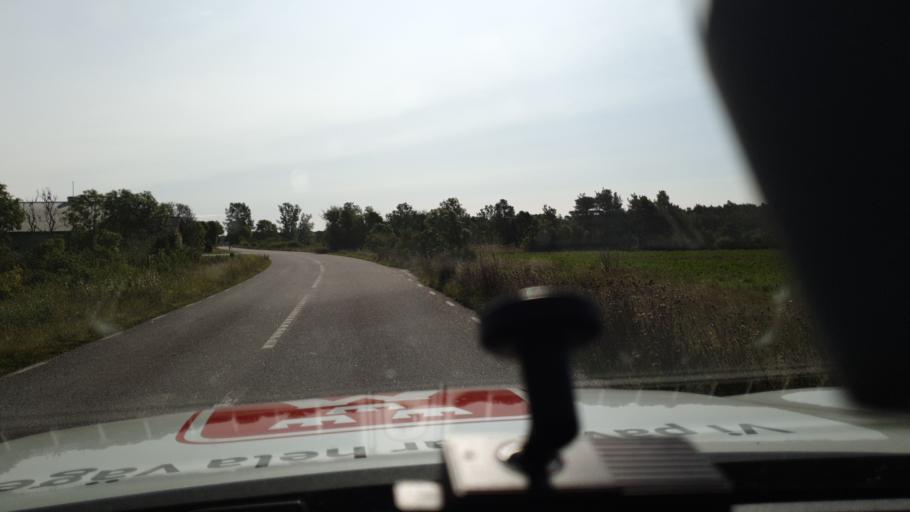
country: SE
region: Gotland
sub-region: Gotland
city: Hemse
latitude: 57.1160
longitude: 18.2772
